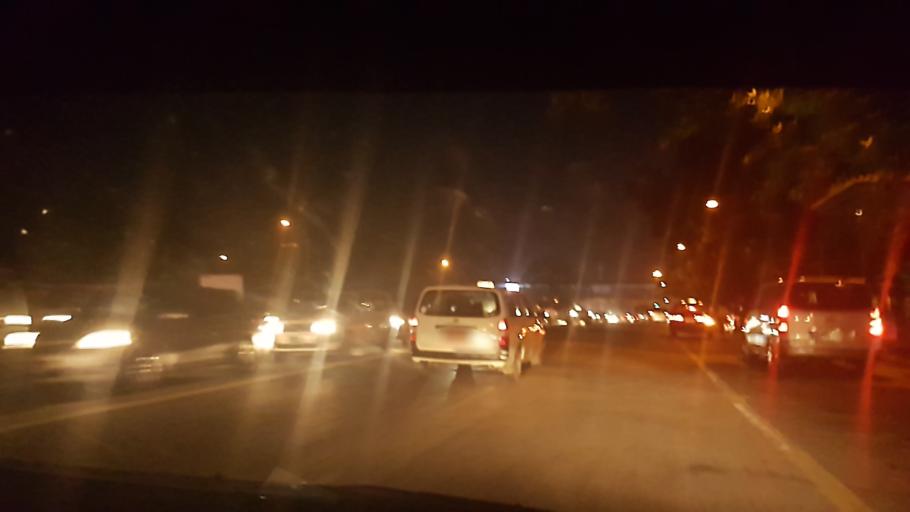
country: MM
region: Yangon
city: Yangon
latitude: 16.7693
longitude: 96.1639
